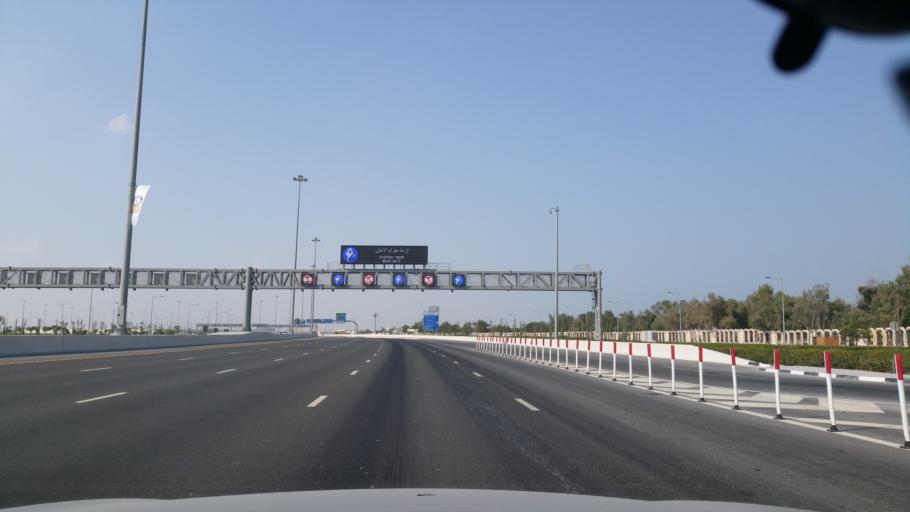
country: QA
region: Baladiyat Umm Salal
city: Umm Salal Muhammad
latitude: 25.3838
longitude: 51.5004
